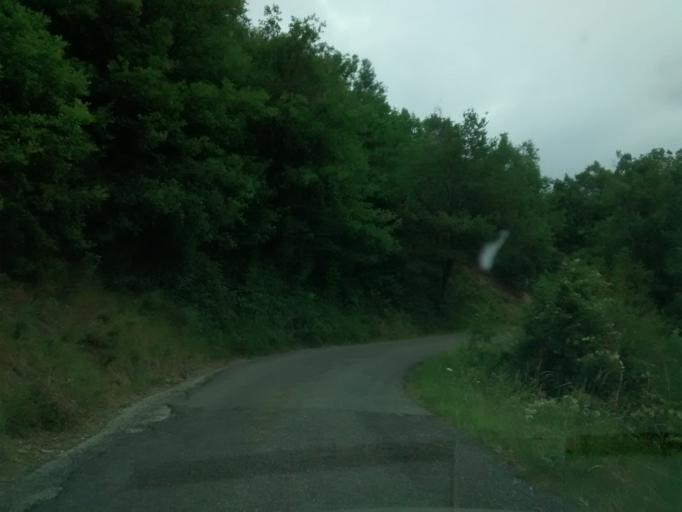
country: ES
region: Aragon
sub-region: Provincia de Huesca
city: Puertolas
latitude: 42.5403
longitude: 0.1335
